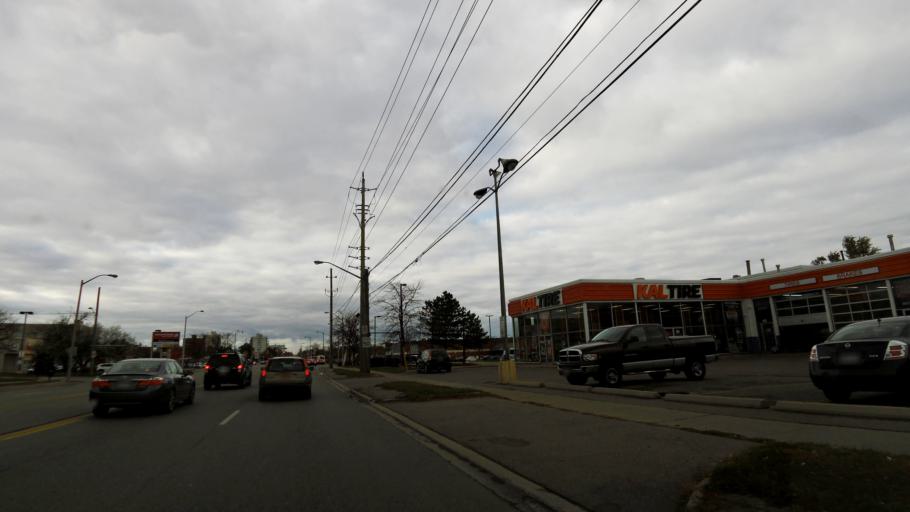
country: CA
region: Ontario
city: Brampton
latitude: 43.6942
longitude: -79.7474
